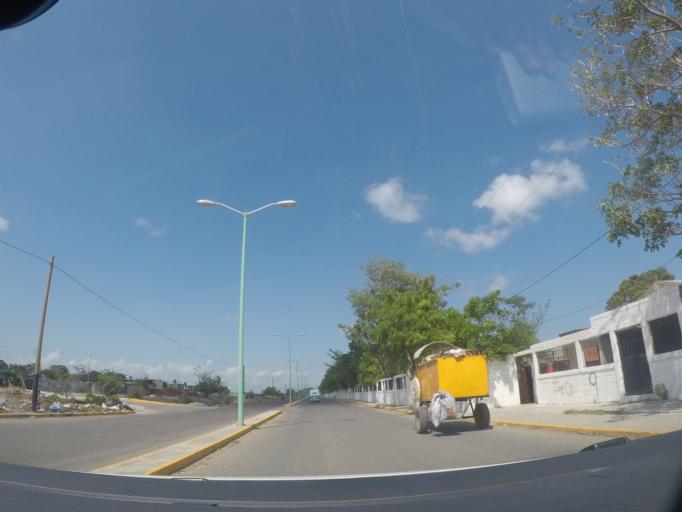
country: MX
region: Oaxaca
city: Juchitan de Zaragoza
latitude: 16.4349
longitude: -95.0108
